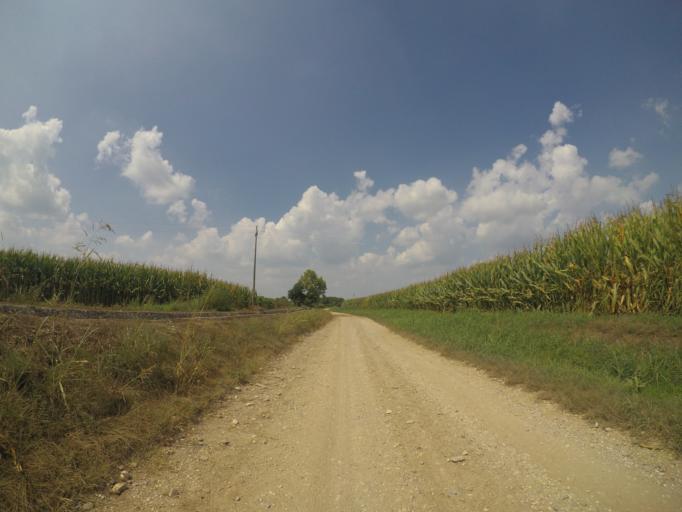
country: IT
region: Friuli Venezia Giulia
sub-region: Provincia di Udine
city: Bertiolo
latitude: 45.9487
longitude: 13.0406
